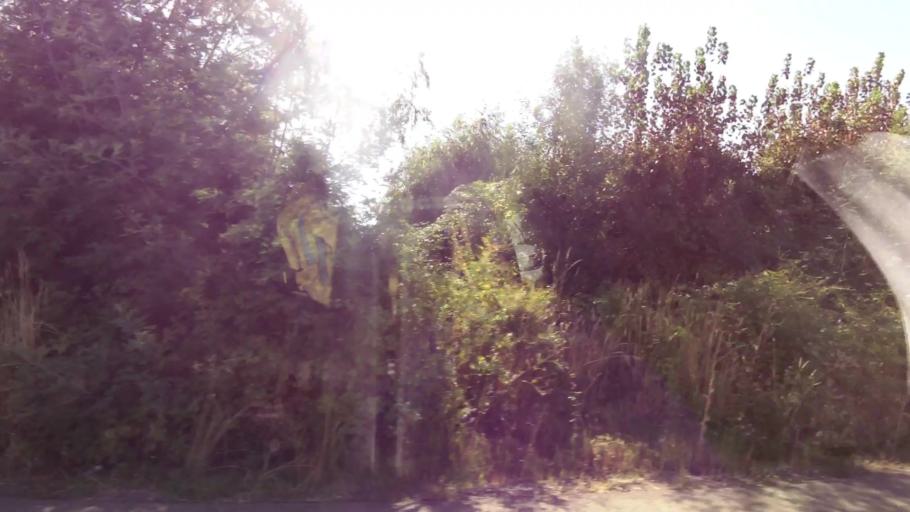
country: CL
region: Maule
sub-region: Provincia de Talca
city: Talca
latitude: -35.4160
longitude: -71.5957
